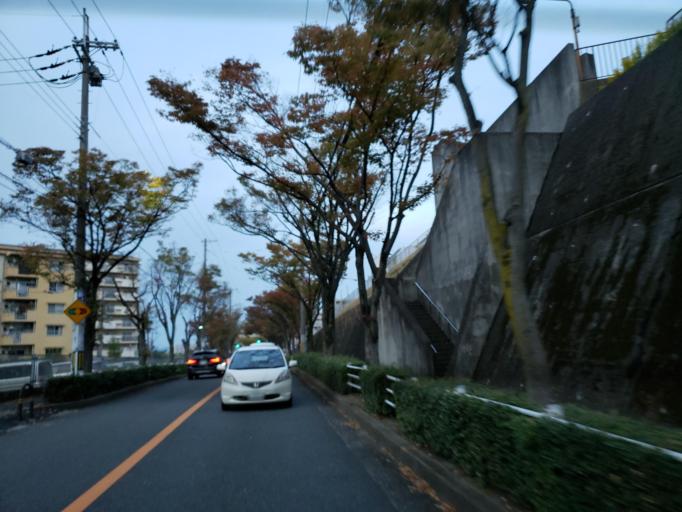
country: JP
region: Osaka
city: Suita
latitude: 34.7920
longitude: 135.5271
